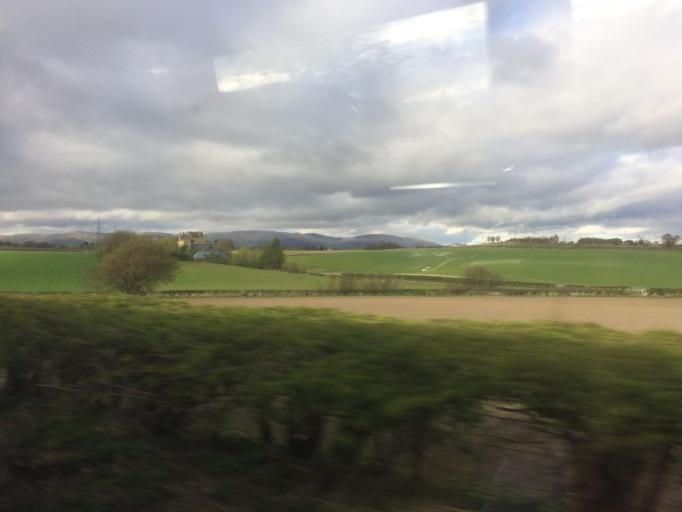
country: GB
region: Scotland
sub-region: Stirling
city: Cowie
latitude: 56.0582
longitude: -3.8501
